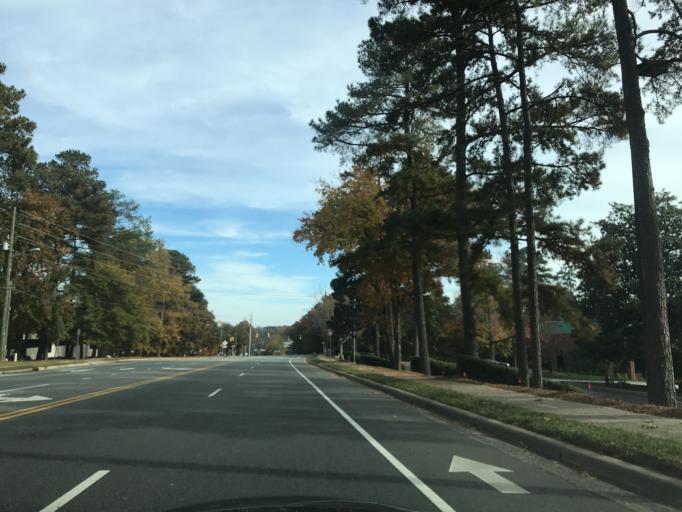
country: US
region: North Carolina
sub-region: Wake County
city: West Raleigh
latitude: 35.8154
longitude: -78.7022
